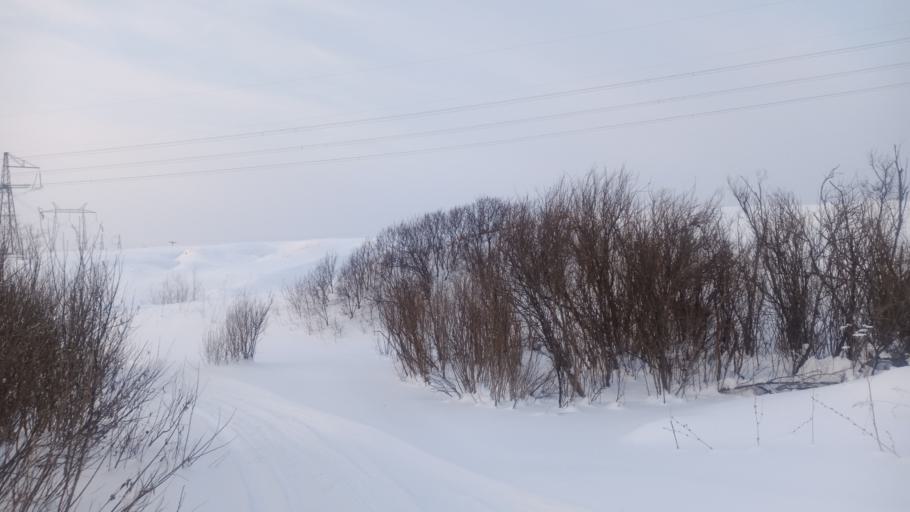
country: RU
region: Altai Krai
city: Nauchnyy Gorodok
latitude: 53.4044
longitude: 83.5142
